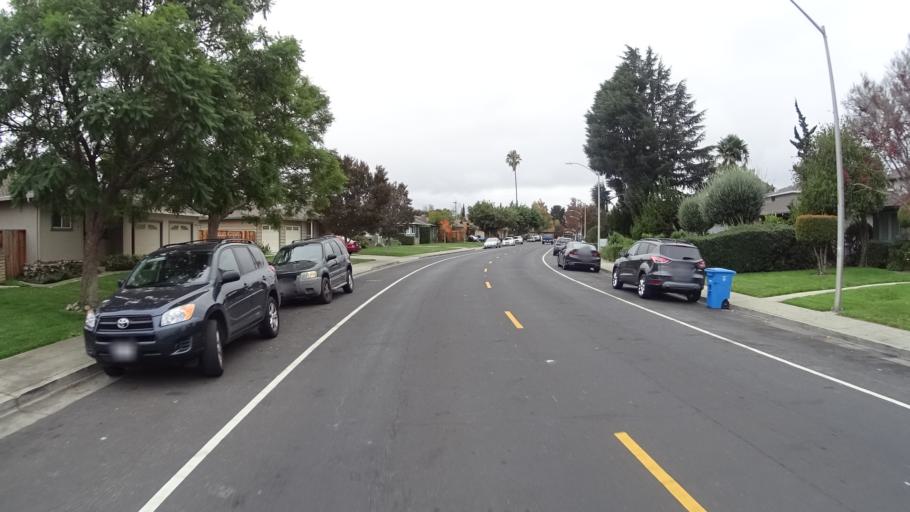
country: US
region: California
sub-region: Santa Clara County
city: Santa Clara
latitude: 37.3366
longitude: -121.9922
